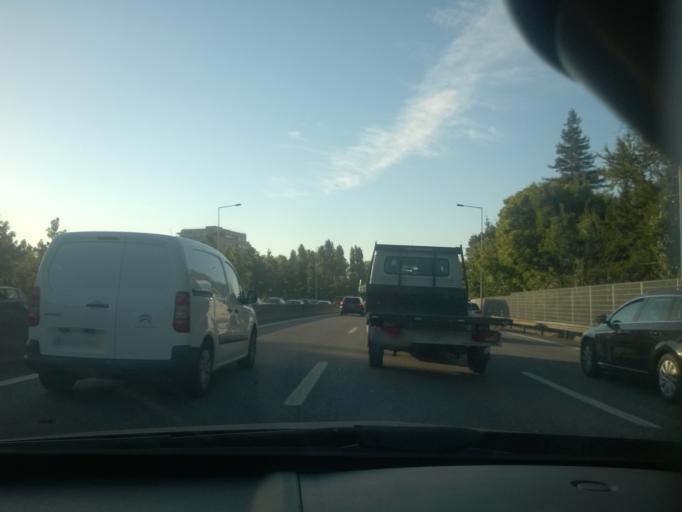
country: PT
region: Porto
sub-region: Vila Nova de Gaia
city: Canidelo
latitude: 41.1523
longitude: -8.6435
